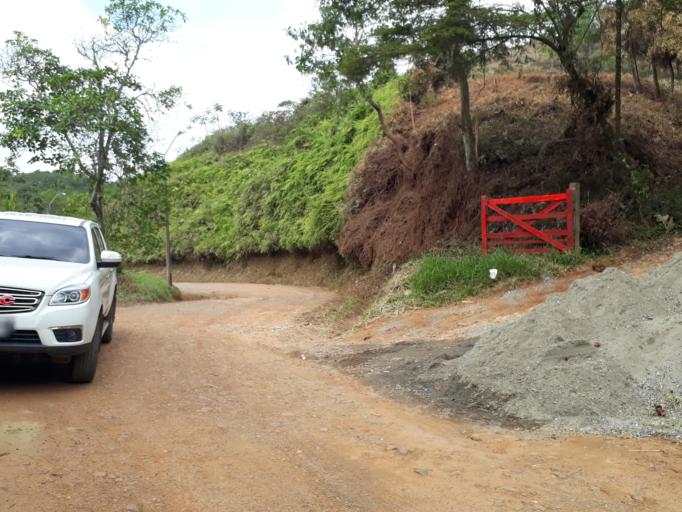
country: CO
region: Valle del Cauca
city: Cali
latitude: 3.3910
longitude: -76.6012
